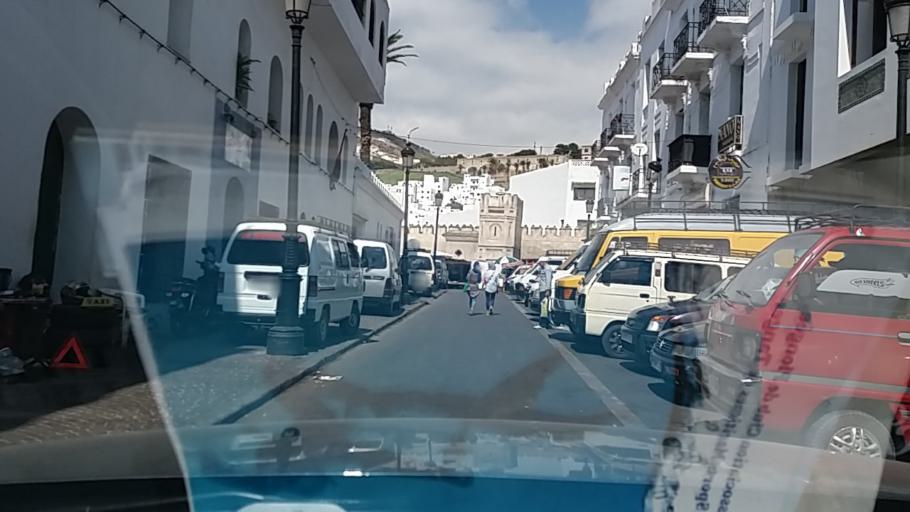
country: MA
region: Tanger-Tetouan
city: Tetouan
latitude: 35.5709
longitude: -5.3723
